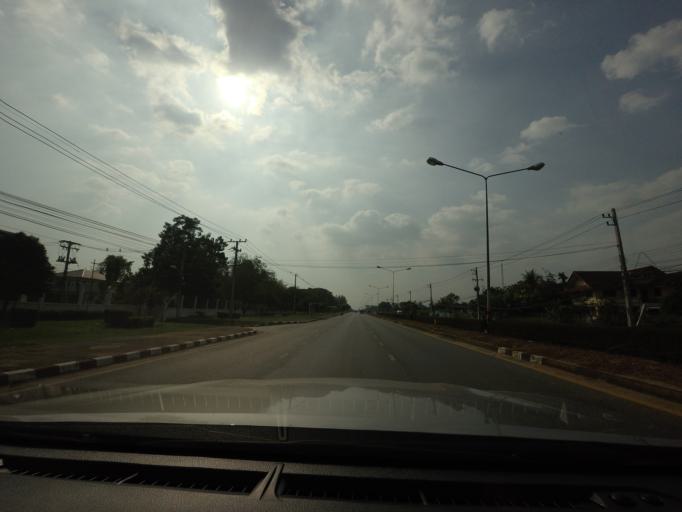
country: TH
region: Sukhothai
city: Sukhothai
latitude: 17.0186
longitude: 99.8579
